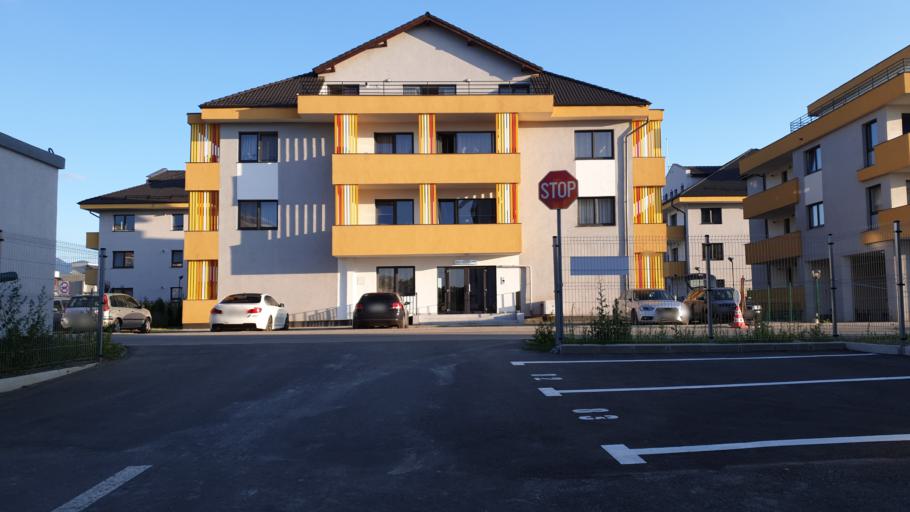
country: RO
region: Brasov
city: Brasov
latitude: 45.6796
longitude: 25.6078
